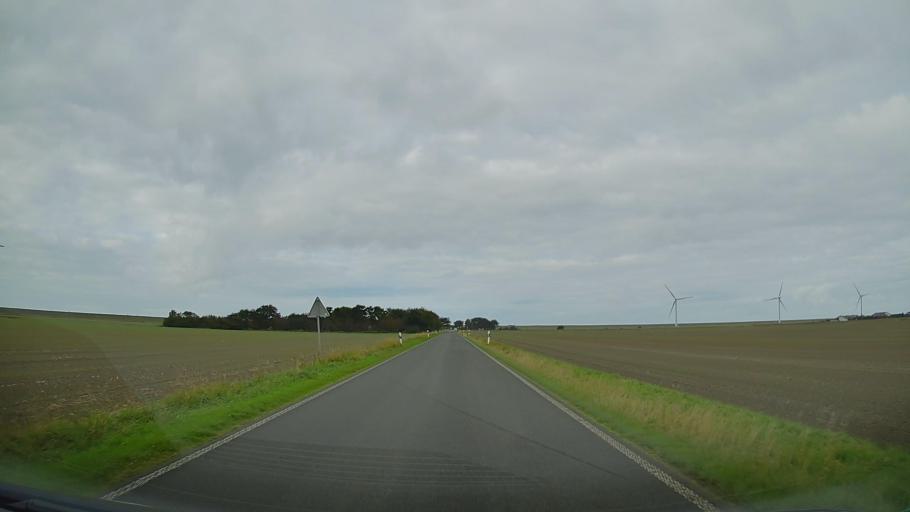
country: DE
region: Schleswig-Holstein
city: Friedrich-Wilhelm-Lubke-Koog
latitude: 54.8379
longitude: 8.6277
